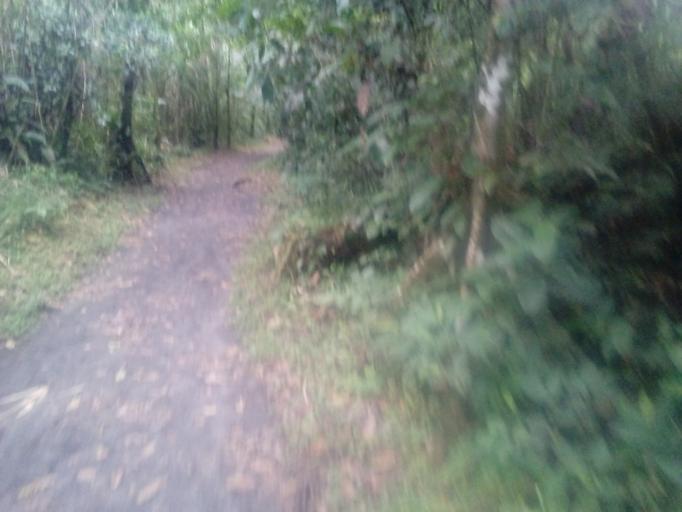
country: CR
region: Alajuela
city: La Fortuna
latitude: 10.4525
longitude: -84.7262
